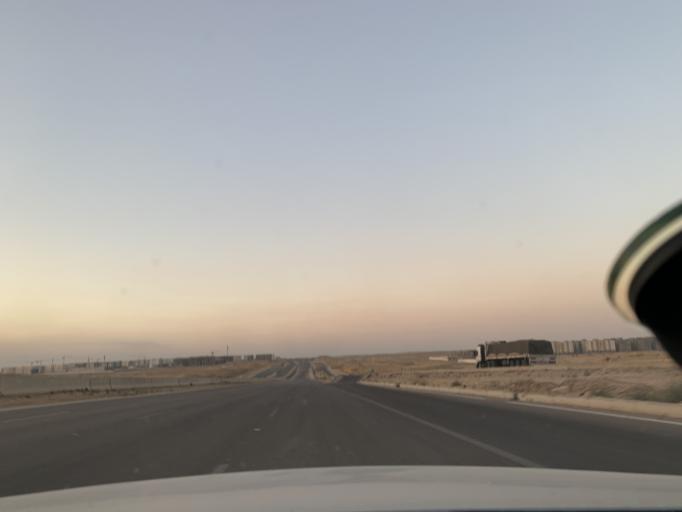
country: EG
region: Muhafazat al Qahirah
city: Halwan
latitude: 29.9553
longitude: 31.5418
